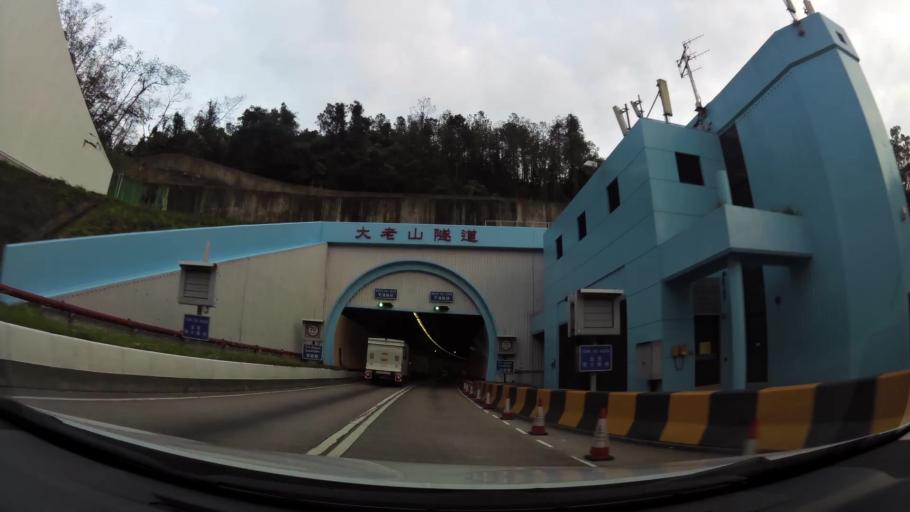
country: HK
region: Sha Tin
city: Sha Tin
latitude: 22.3767
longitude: 114.2140
